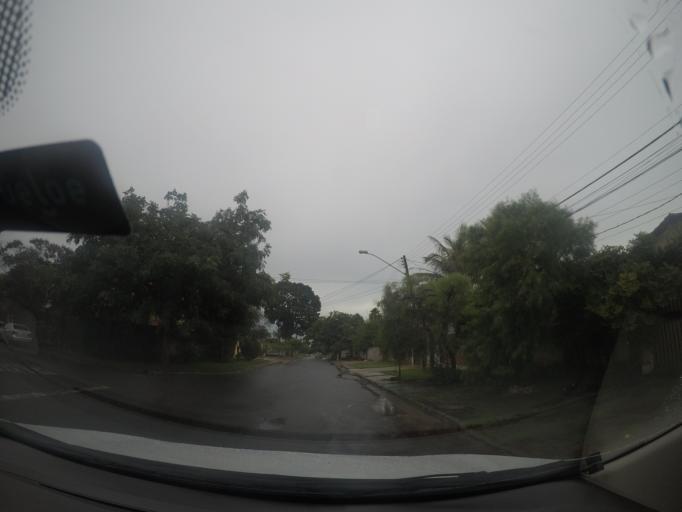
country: BR
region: Goias
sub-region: Goiania
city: Goiania
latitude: -16.6357
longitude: -49.2307
